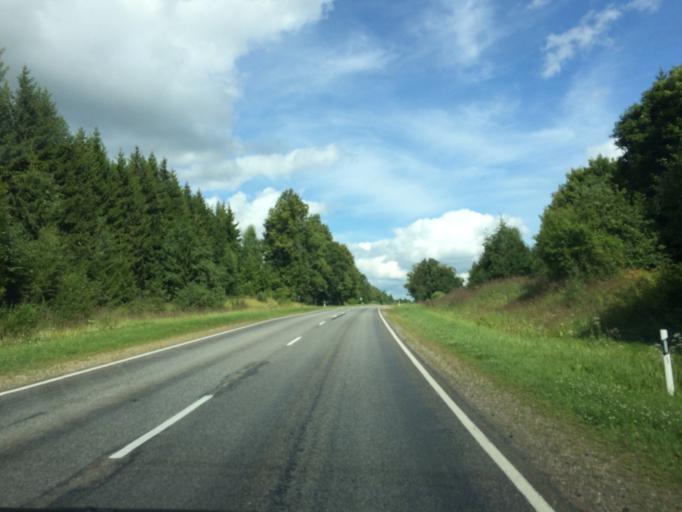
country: LV
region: Rezekne
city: Rezekne
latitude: 56.6282
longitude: 27.4625
